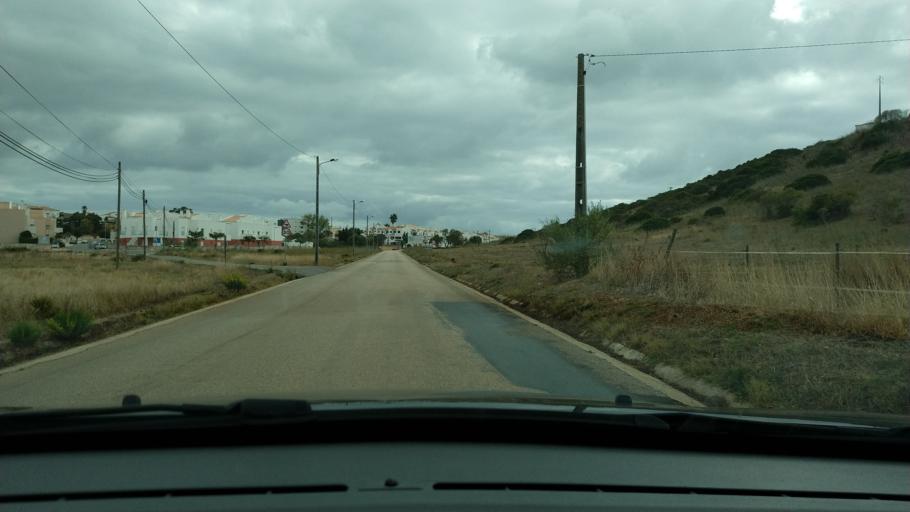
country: PT
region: Faro
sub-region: Lagos
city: Lagos
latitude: 37.0783
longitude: -8.7760
